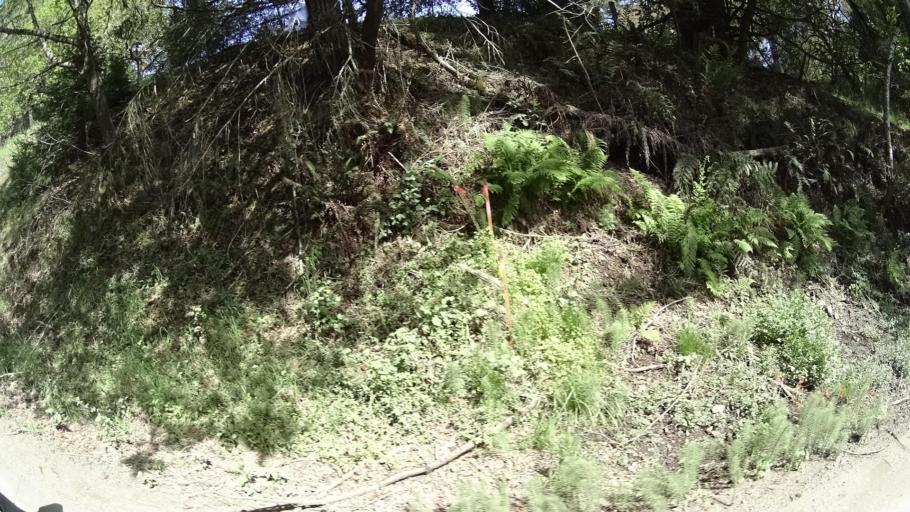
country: US
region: California
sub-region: Humboldt County
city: Redway
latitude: 40.4015
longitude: -123.7465
